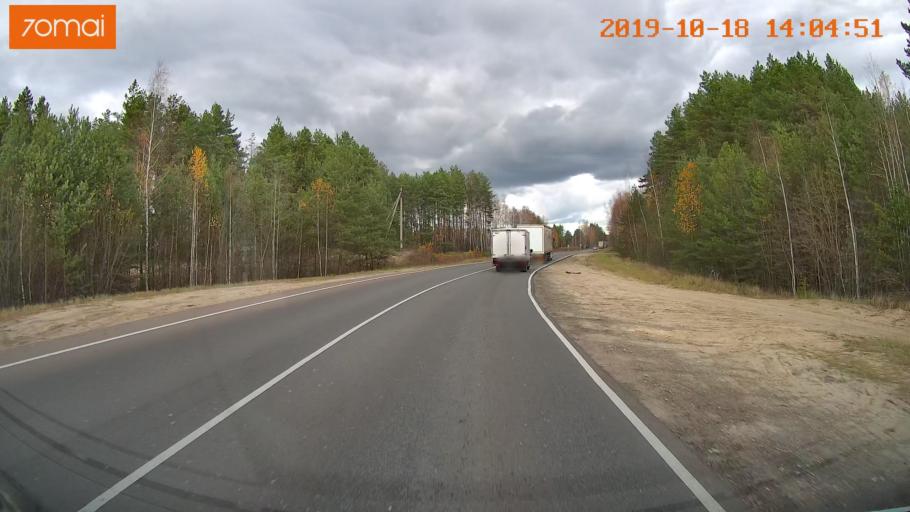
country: RU
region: Rjazan
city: Spas-Klepiki
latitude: 55.1300
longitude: 40.1339
